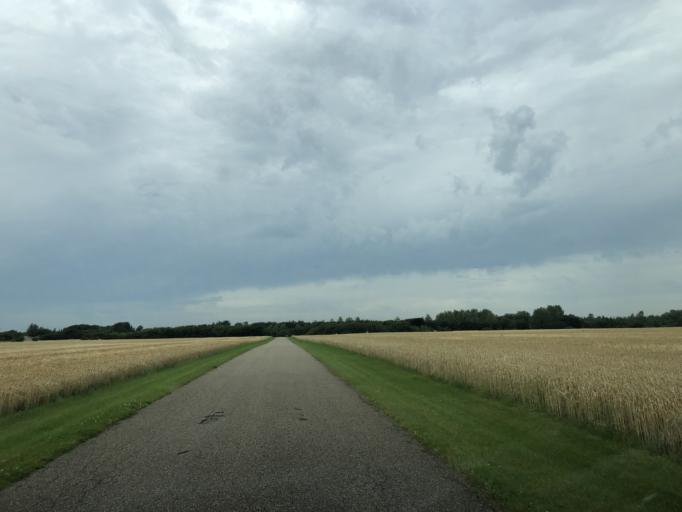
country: DK
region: Central Jutland
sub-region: Holstebro Kommune
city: Ulfborg
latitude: 56.3632
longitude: 8.4440
